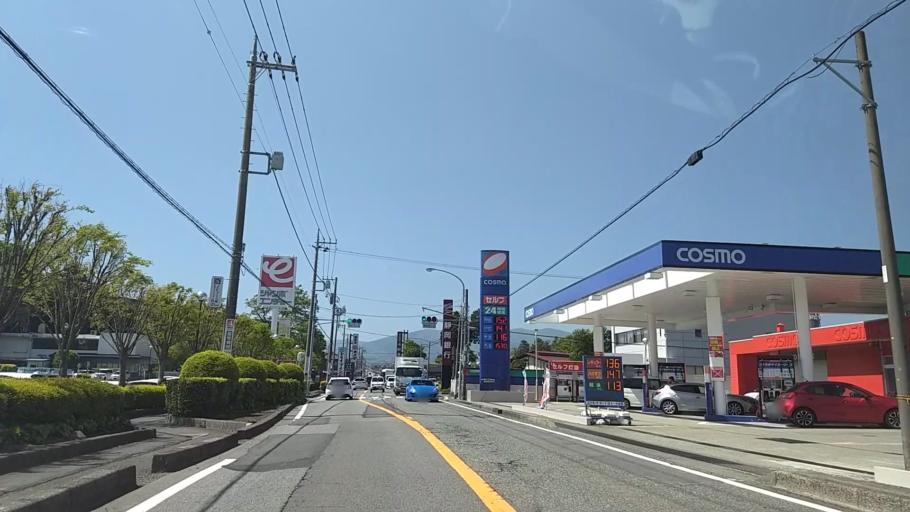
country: JP
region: Shizuoka
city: Gotemba
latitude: 35.2974
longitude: 138.9423
